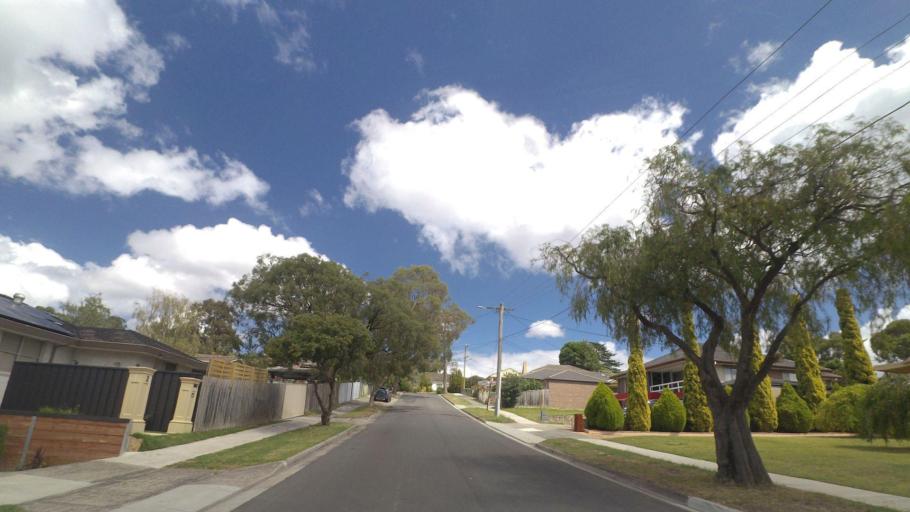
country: AU
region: Victoria
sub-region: Knox
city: Boronia
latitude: -37.8660
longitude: 145.2922
